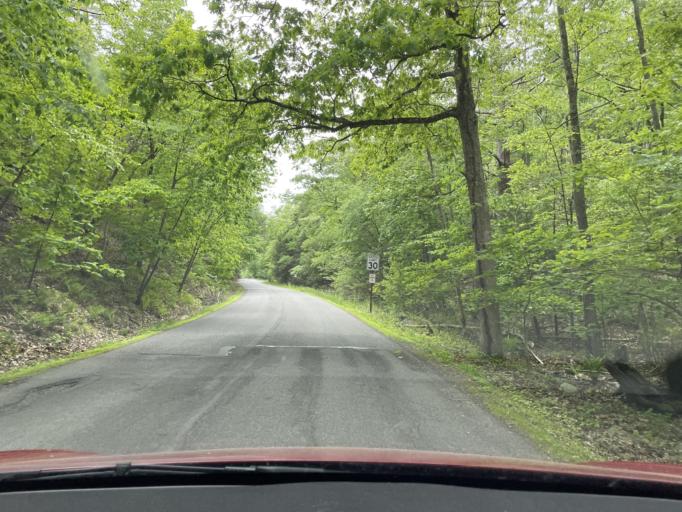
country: US
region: New York
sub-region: Ulster County
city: Zena
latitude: 41.9762
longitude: -74.0676
